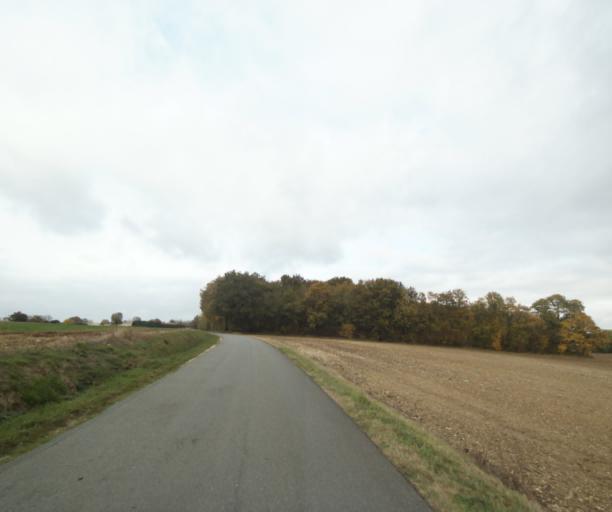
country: FR
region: Poitou-Charentes
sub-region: Departement de la Charente-Maritime
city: Saint-Georges-des-Coteaux
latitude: 45.7827
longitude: -0.7211
